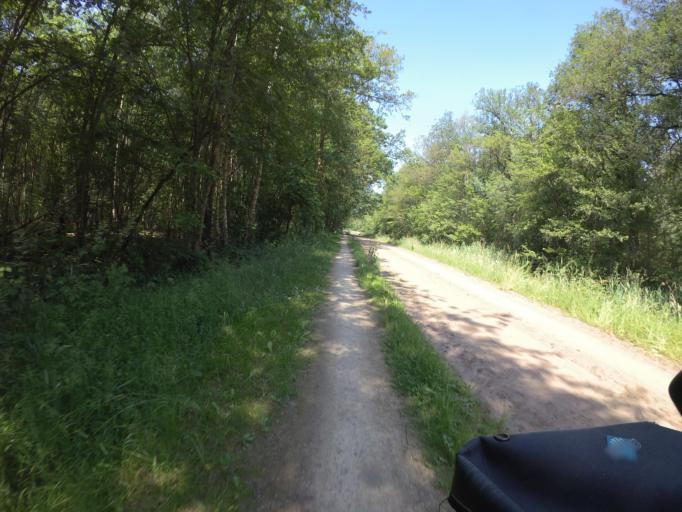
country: NL
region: Gelderland
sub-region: Berkelland
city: Neede
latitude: 52.1549
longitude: 6.6246
